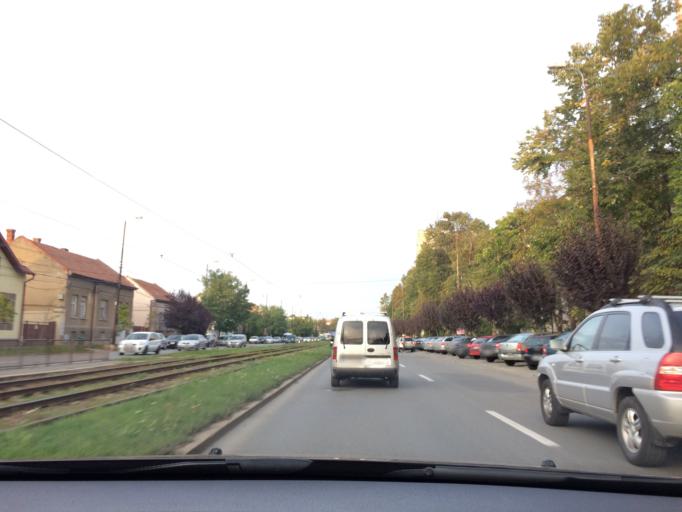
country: RO
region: Timis
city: Timisoara
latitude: 45.7655
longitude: 21.2132
